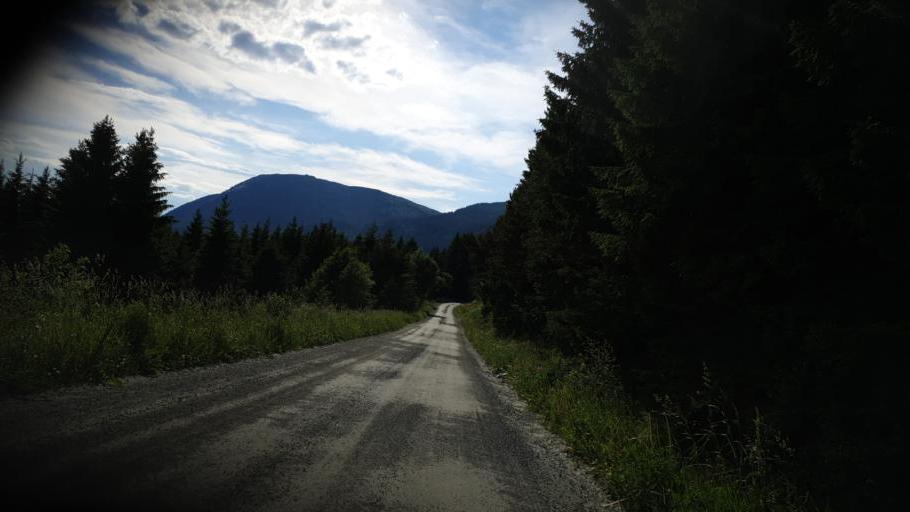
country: NO
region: Sor-Trondelag
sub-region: Trondheim
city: Trondheim
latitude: 63.5755
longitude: 10.3870
